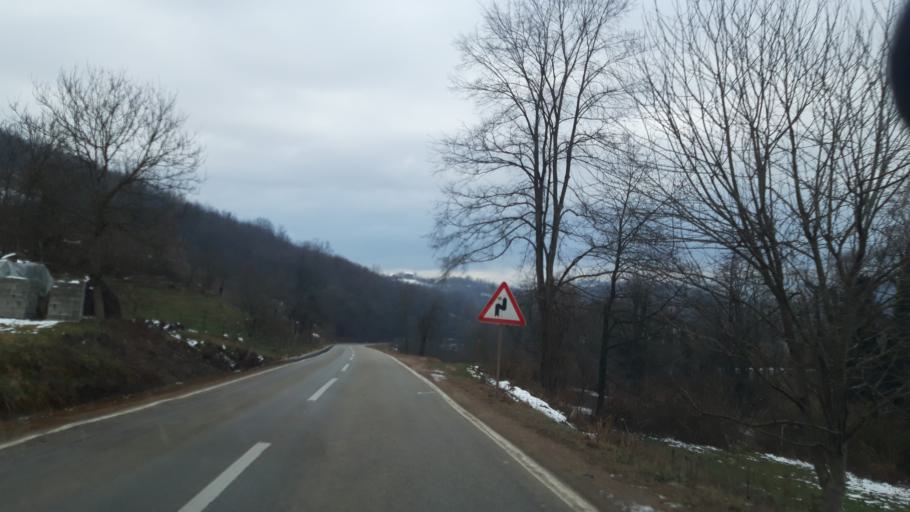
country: BA
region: Republika Srpska
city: Milici
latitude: 44.2323
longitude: 19.1042
